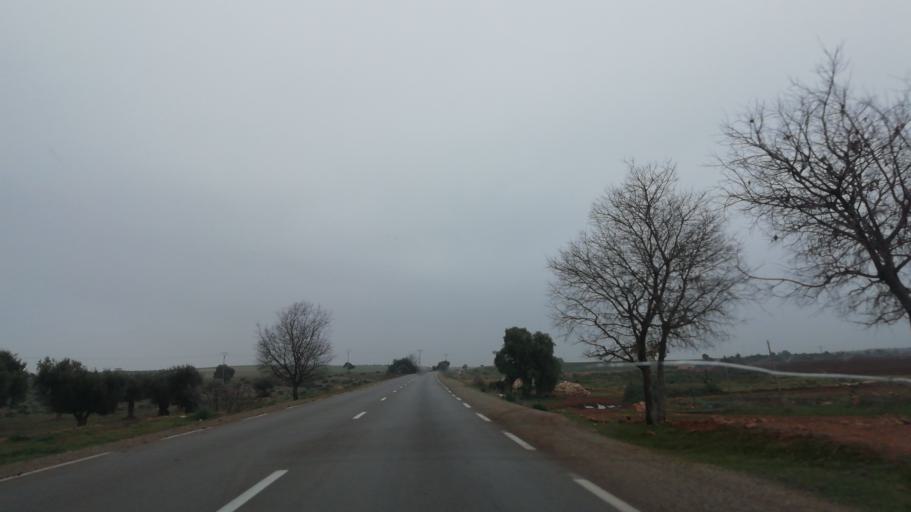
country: DZ
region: Mascara
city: Mascara
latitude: 35.3078
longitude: 0.4129
